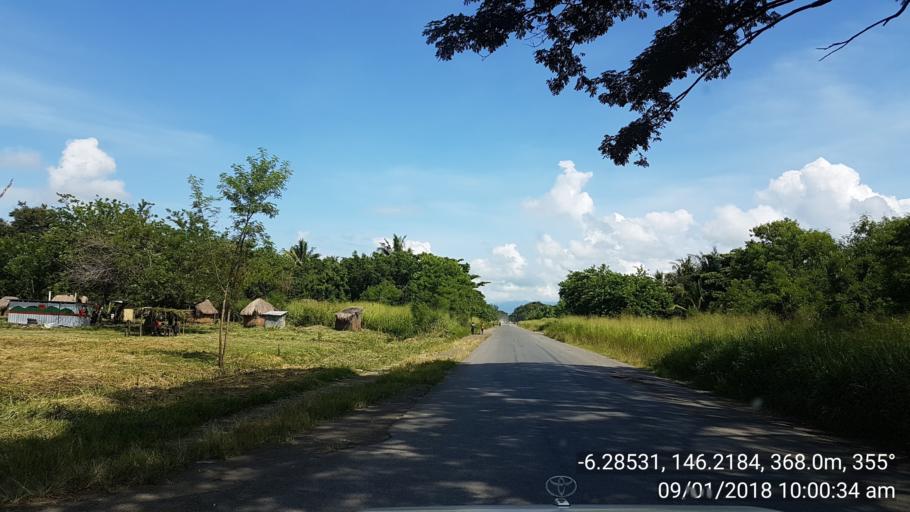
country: PG
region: Eastern Highlands
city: Kainantu
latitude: -6.2853
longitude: 146.2183
